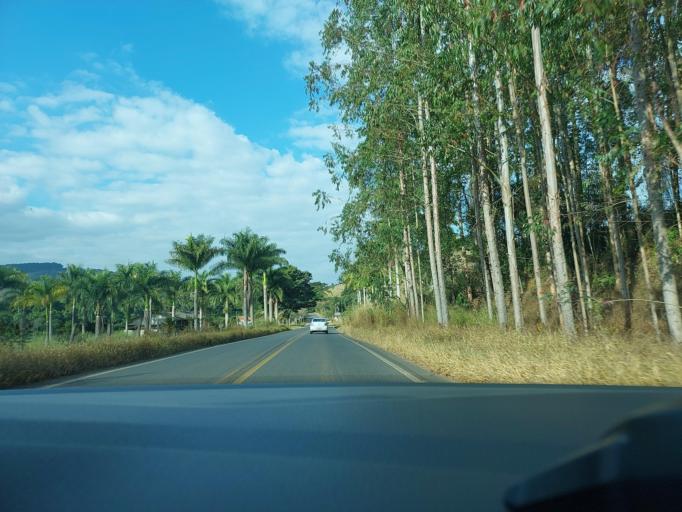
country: BR
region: Minas Gerais
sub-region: Vicosa
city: Vicosa
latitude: -20.8273
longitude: -42.7805
